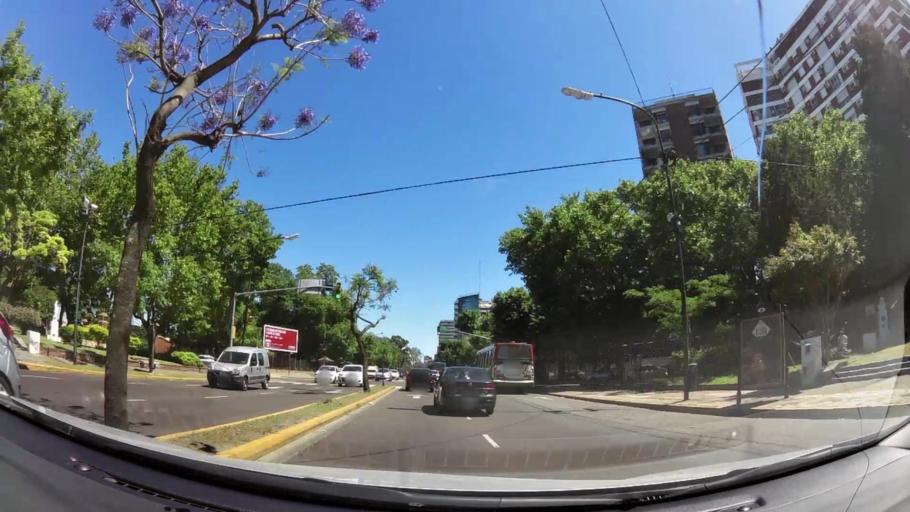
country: AR
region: Buenos Aires
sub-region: Partido de San Isidro
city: San Isidro
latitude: -34.4803
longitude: -58.5069
